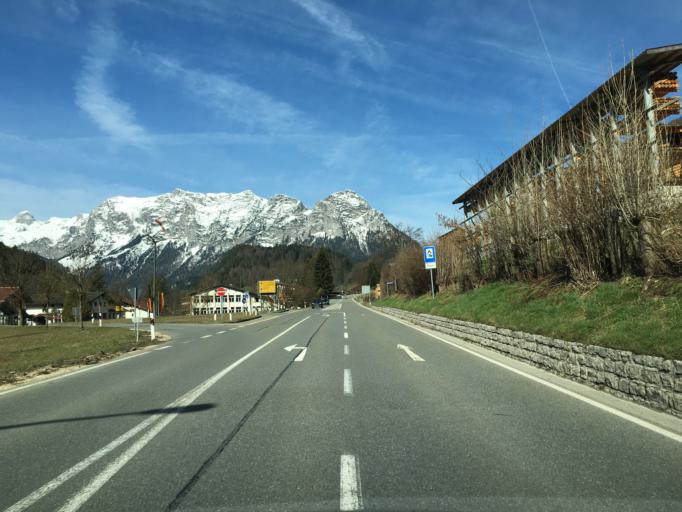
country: DE
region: Bavaria
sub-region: Upper Bavaria
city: Ramsau
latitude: 47.6055
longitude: 12.9115
